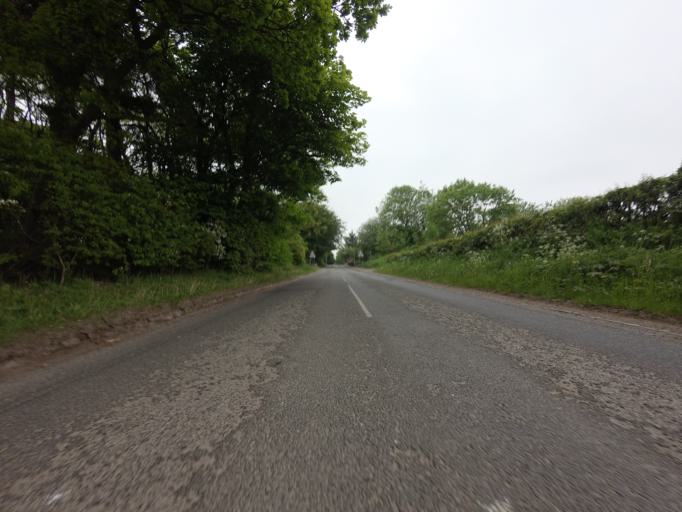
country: GB
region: Scotland
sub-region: Fife
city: Townhill
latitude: 56.0943
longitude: -3.4420
